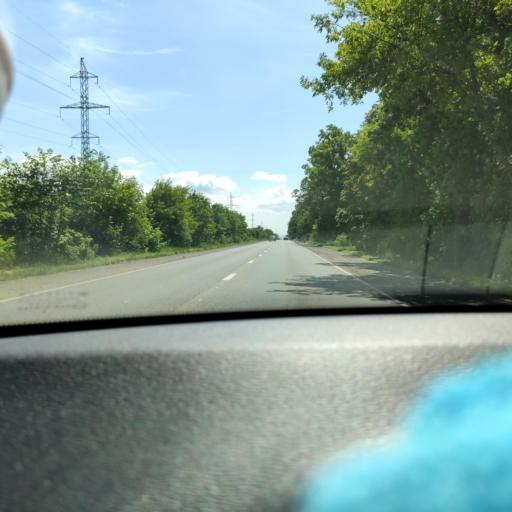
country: RU
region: Samara
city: Novosemeykino
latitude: 53.3388
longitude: 50.2497
